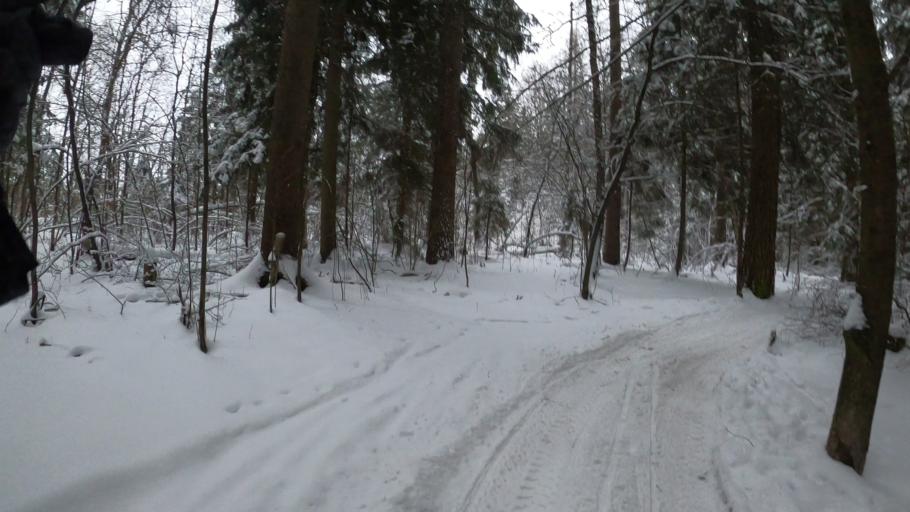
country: RU
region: Moskovskaya
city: Firsanovka
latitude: 55.9319
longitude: 37.2209
